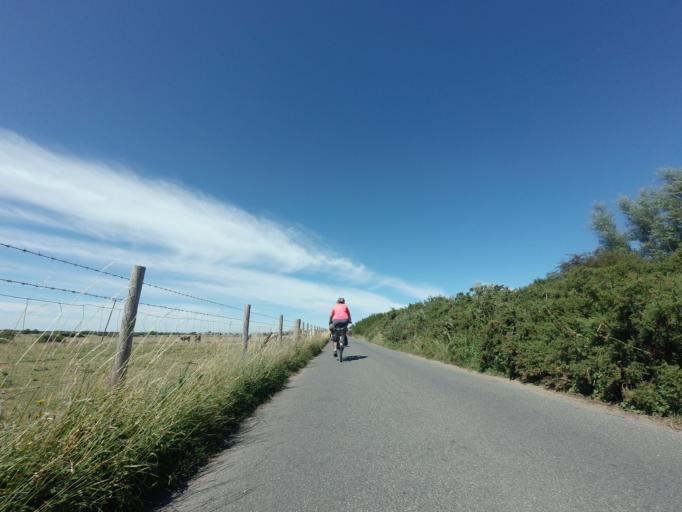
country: GB
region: England
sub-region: Kent
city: Deal
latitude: 51.2450
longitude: 1.3955
